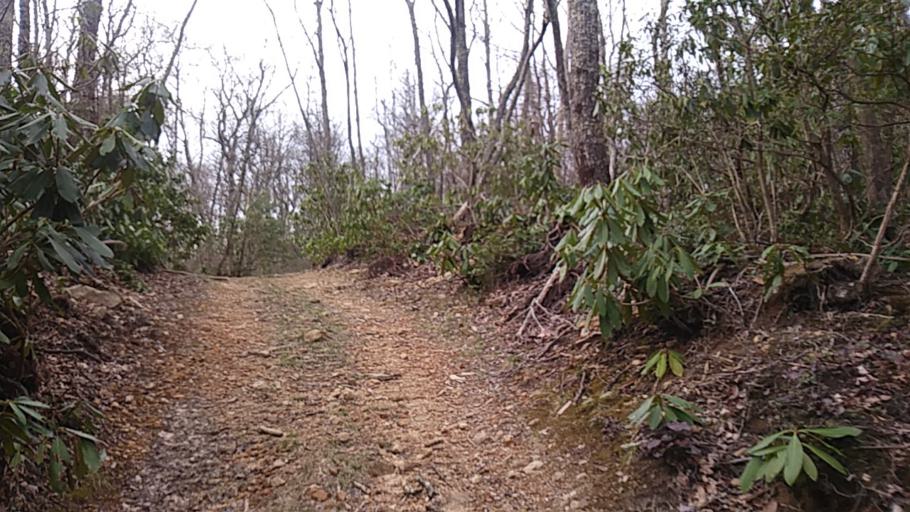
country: US
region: Tennessee
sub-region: Greene County
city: Tusculum
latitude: 36.0597
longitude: -82.6755
